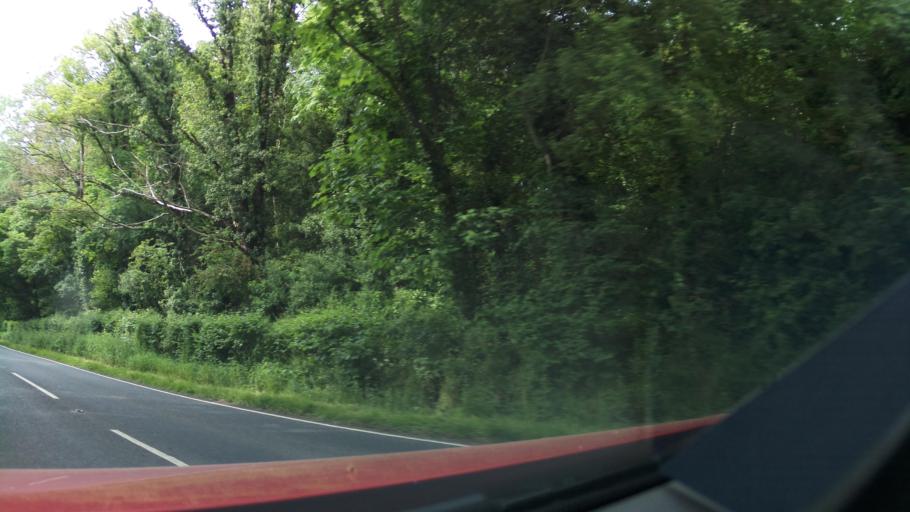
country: GB
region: England
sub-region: Worcestershire
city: Evesham
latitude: 52.1058
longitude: -1.9539
